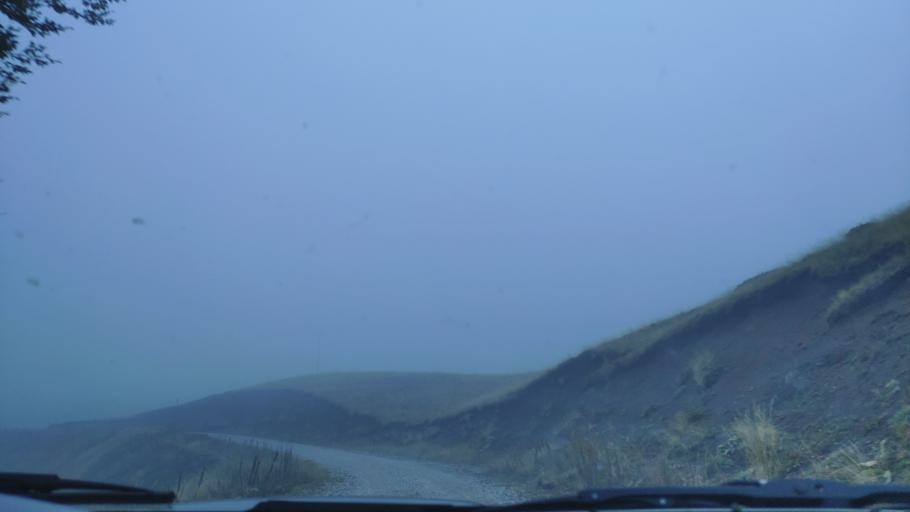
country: GR
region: West Macedonia
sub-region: Nomos Kastorias
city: Nestorio
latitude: 40.2983
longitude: 20.9189
